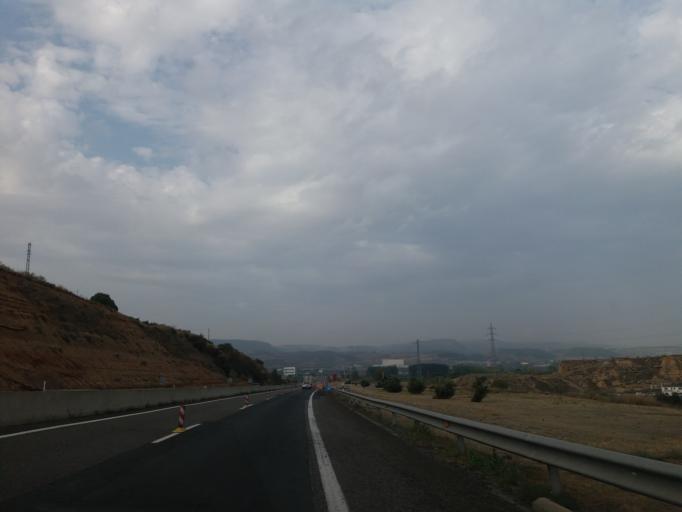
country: ES
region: Aragon
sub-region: Provincia de Huesca
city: Fraga
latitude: 41.5089
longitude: 0.3583
